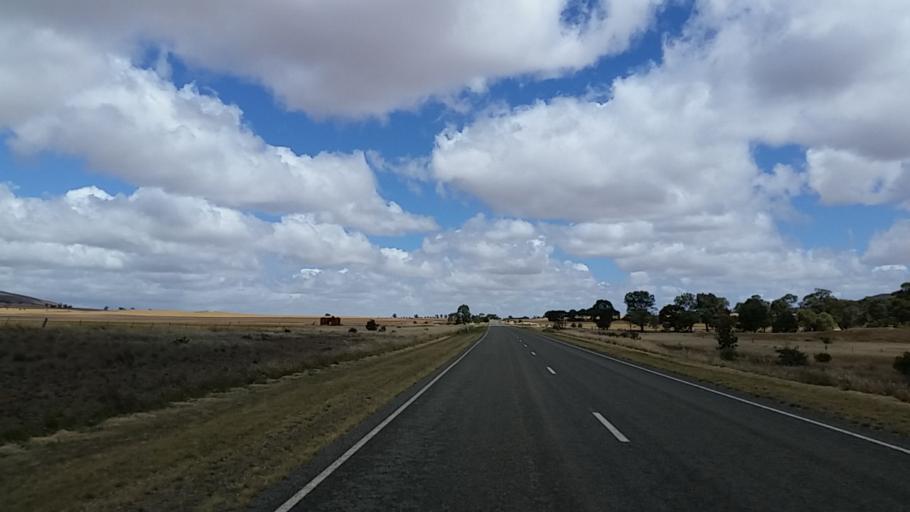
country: AU
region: South Australia
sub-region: Peterborough
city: Peterborough
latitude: -32.8600
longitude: 138.5425
